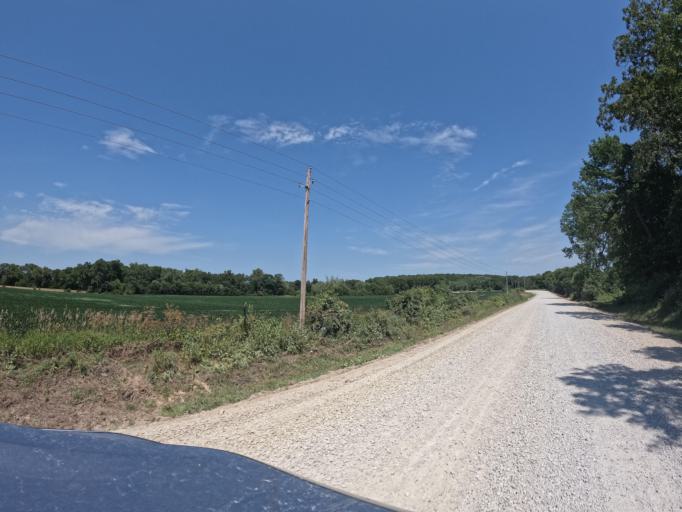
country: US
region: Iowa
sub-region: Henry County
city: Mount Pleasant
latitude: 40.9047
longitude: -91.6752
